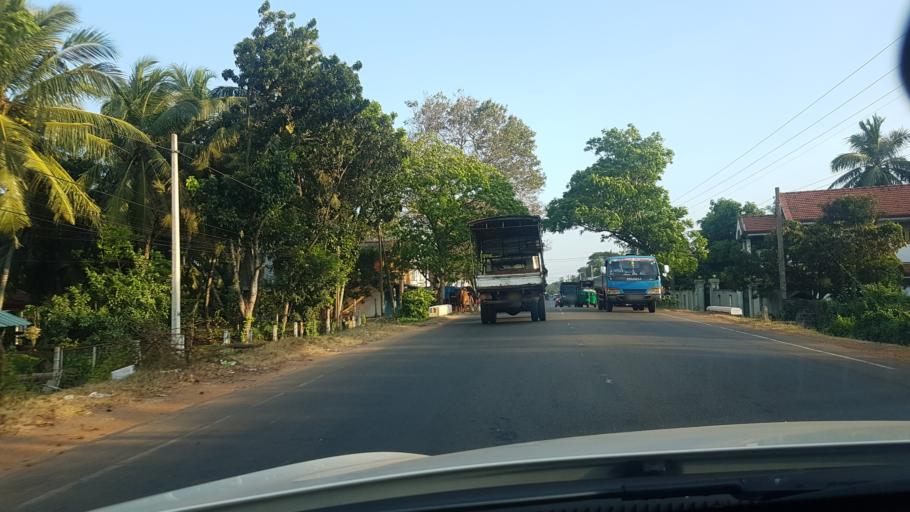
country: LK
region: North Western
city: Chilaw
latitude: 7.5649
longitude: 79.8024
